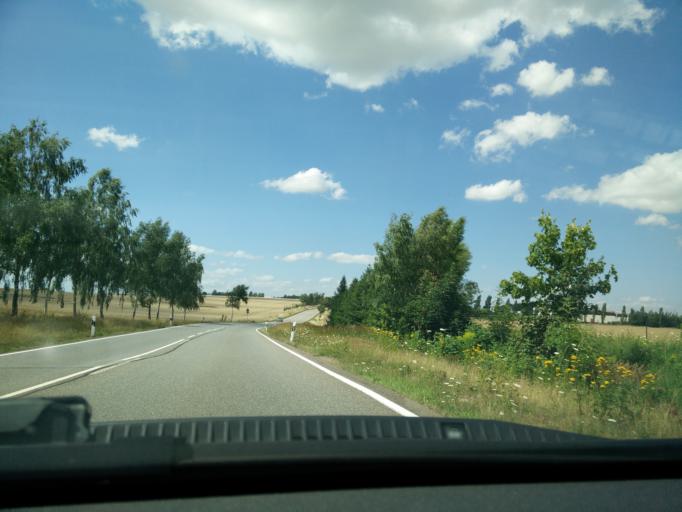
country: DE
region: Saxony
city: Hartmannsdorf
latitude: 50.8938
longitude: 12.7860
